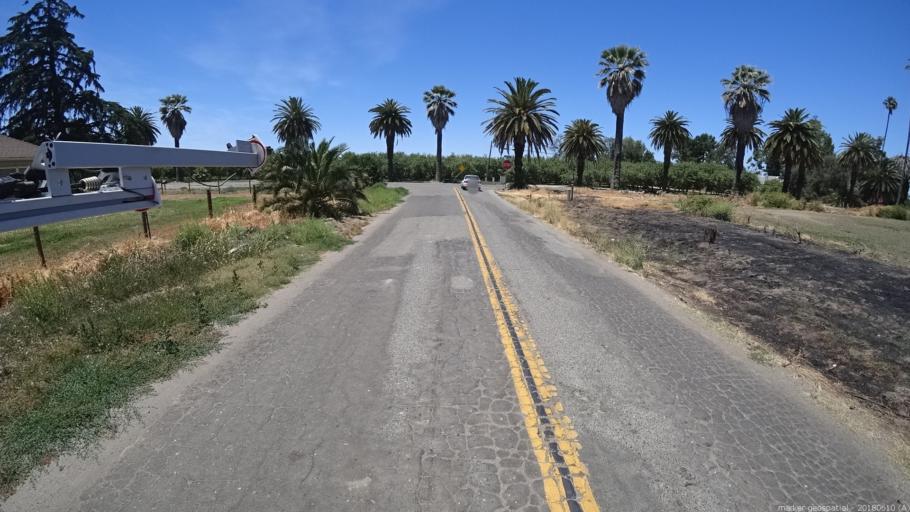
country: US
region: California
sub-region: Madera County
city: Chowchilla
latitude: 37.0783
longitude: -120.3013
